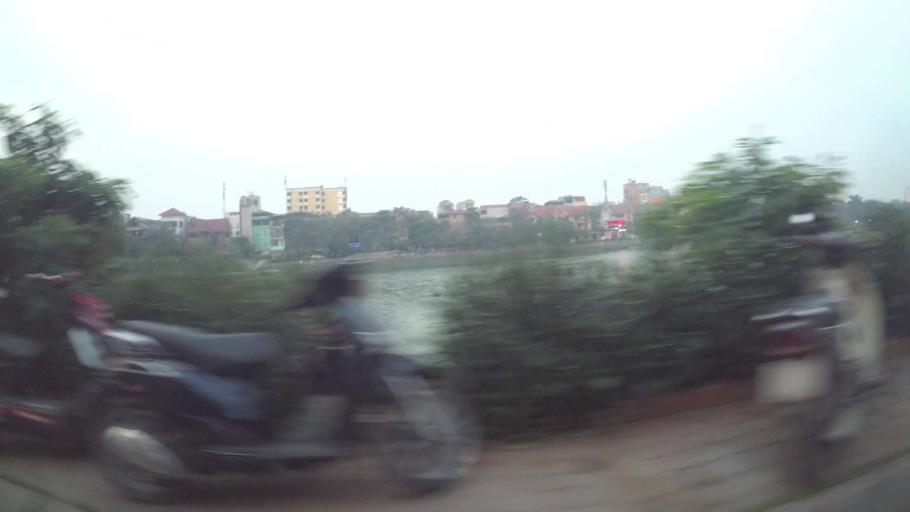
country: VN
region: Ha Noi
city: Ha Dong
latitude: 20.9783
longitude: 105.7899
